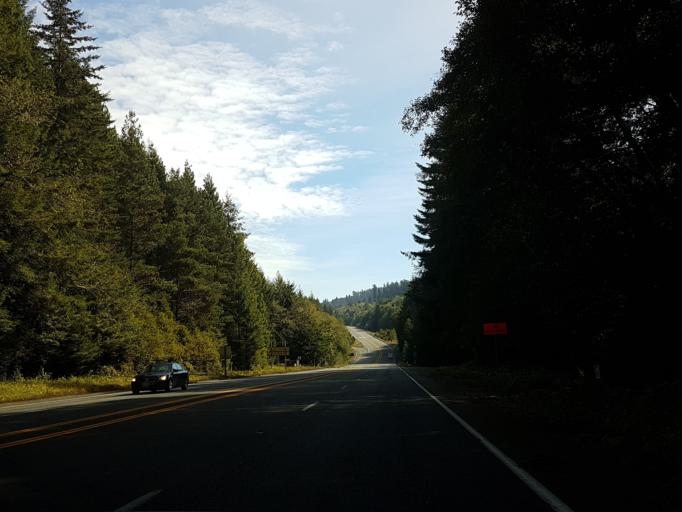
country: US
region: California
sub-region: Del Norte County
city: Bertsch-Oceanview
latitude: 41.4730
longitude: -124.0434
